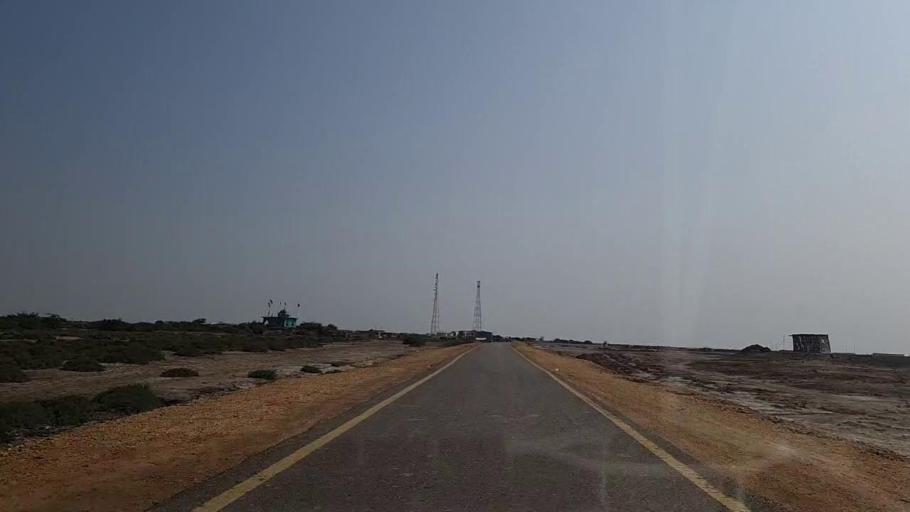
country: PK
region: Sindh
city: Chuhar Jamali
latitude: 24.1683
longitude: 67.8961
